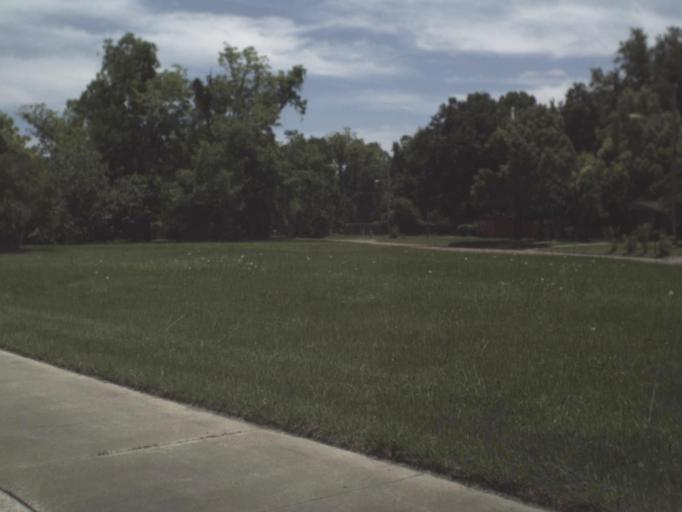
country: US
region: Florida
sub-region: Duval County
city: Jacksonville
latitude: 30.3527
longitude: -81.7064
